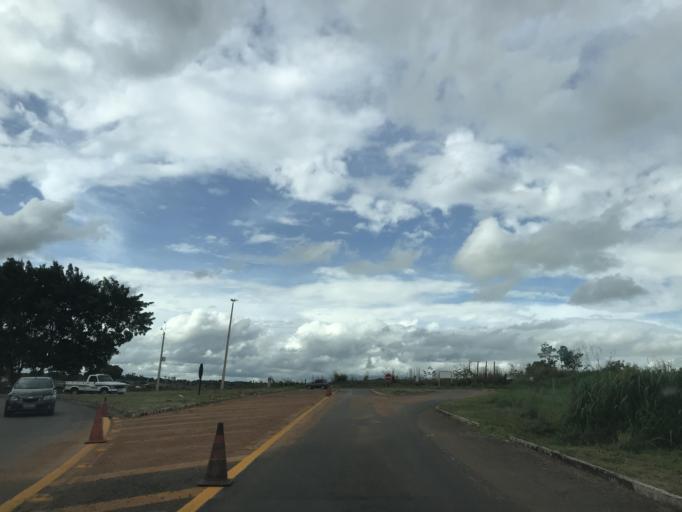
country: BR
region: Goias
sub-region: Bela Vista De Goias
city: Bela Vista de Goias
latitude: -17.0599
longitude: -48.6576
